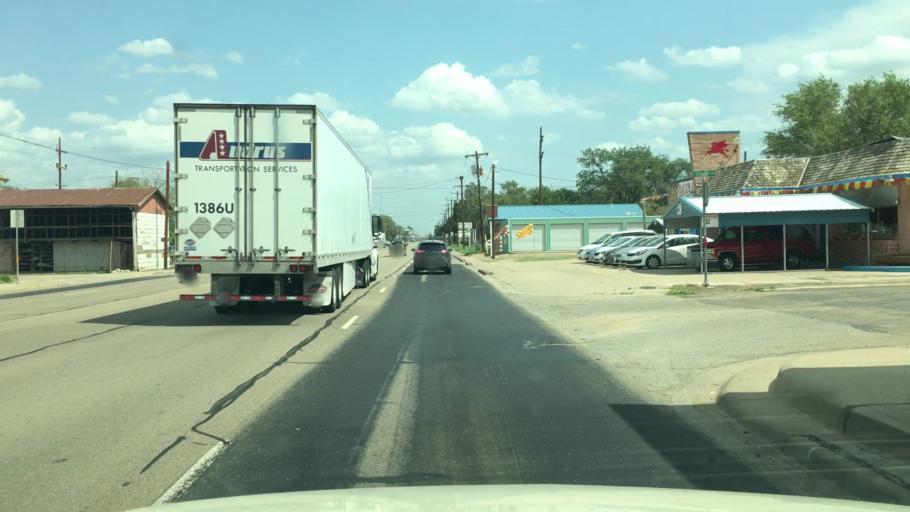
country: US
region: Texas
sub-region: Donley County
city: Clarendon
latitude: 34.9372
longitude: -100.8864
